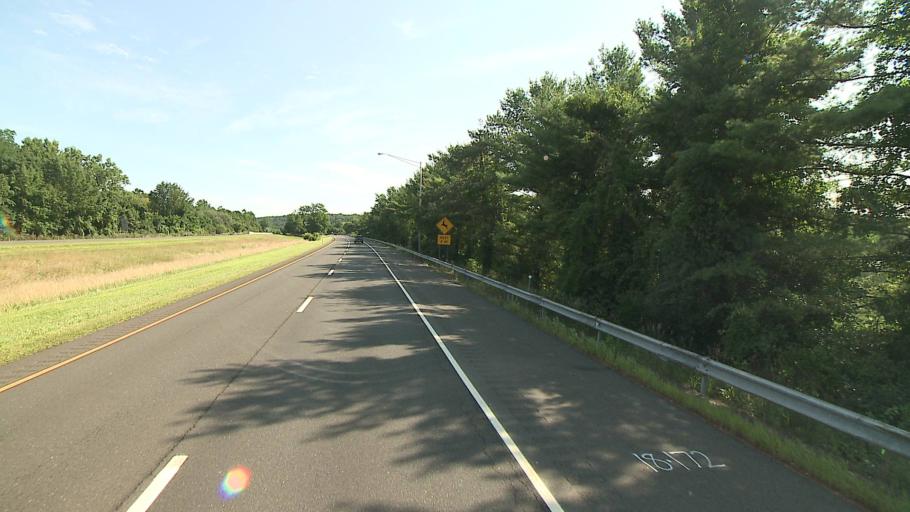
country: US
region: Connecticut
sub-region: Fairfield County
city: Bethel
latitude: 41.4371
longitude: -73.4019
